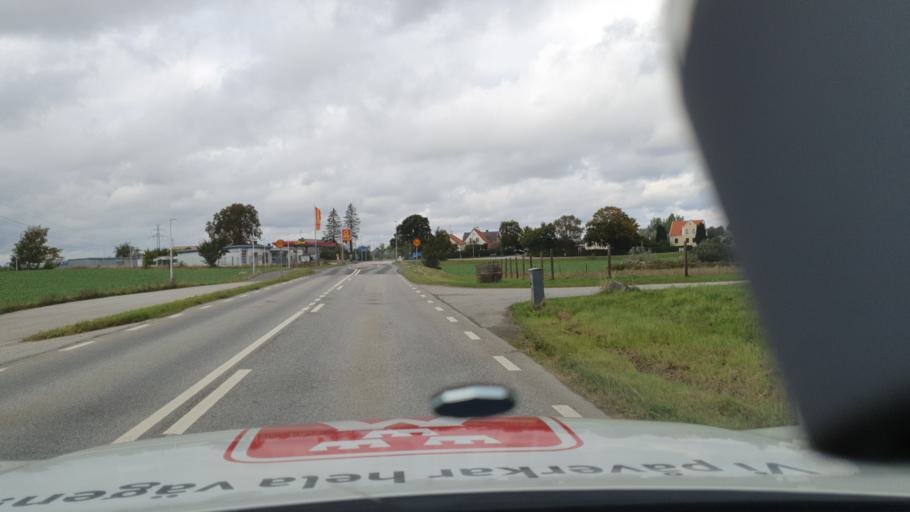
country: SE
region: Skane
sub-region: Malmo
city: Oxie
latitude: 55.5155
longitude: 13.0899
